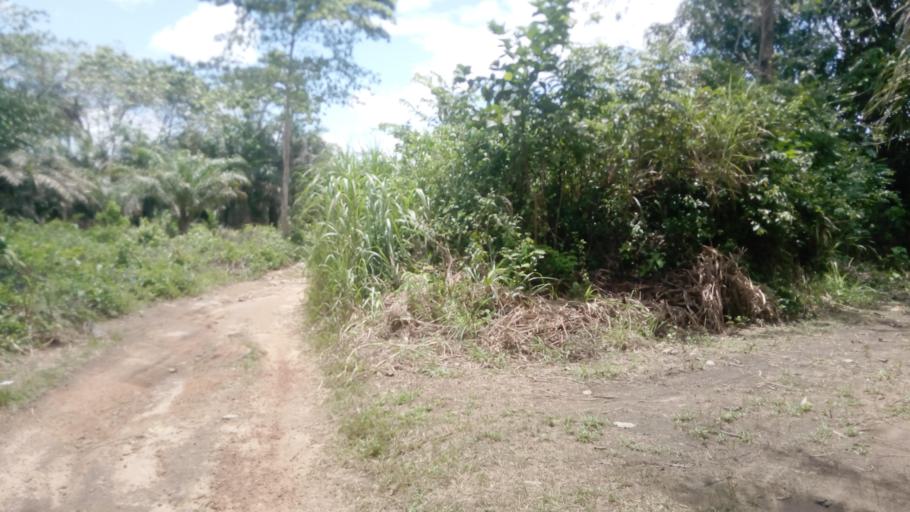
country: SL
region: Northern Province
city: Binkolo
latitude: 8.9245
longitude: -12.0091
